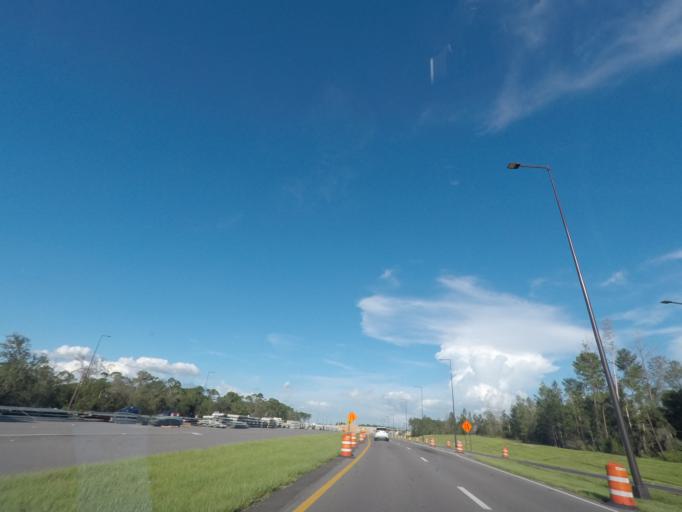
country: US
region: Florida
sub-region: Osceola County
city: Celebration
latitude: 28.3482
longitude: -81.5607
